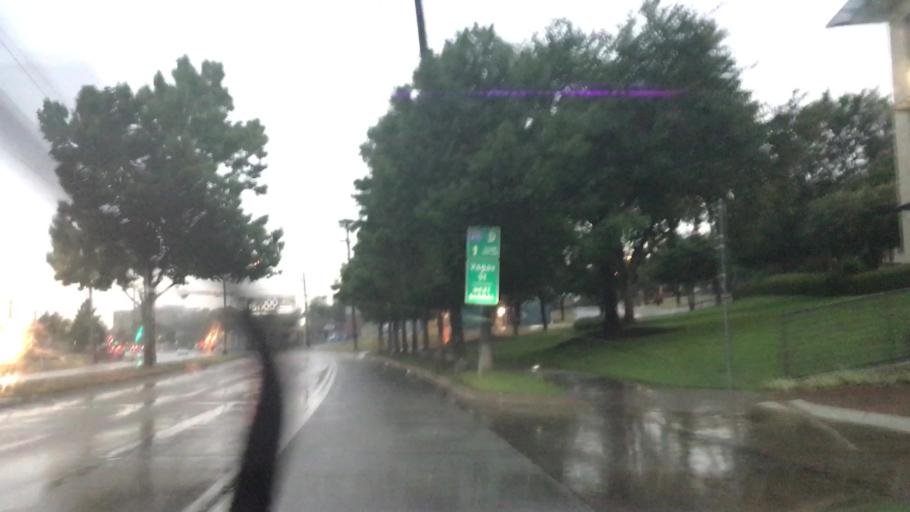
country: US
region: Texas
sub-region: Dallas County
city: Dallas
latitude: 32.8041
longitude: -96.8205
